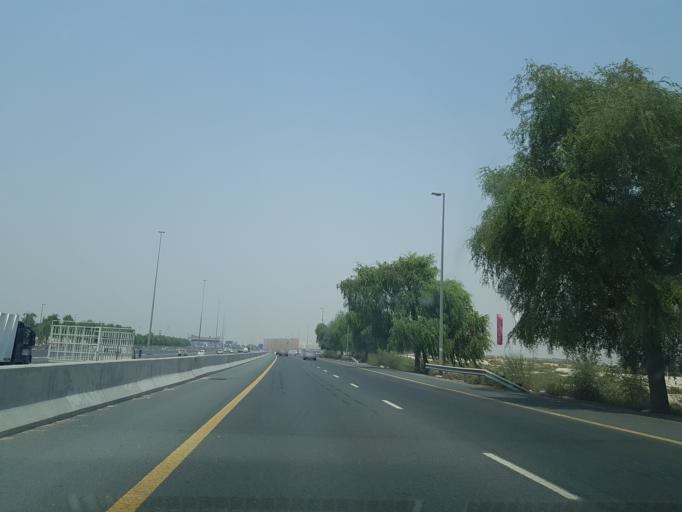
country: AE
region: Ash Shariqah
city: Sharjah
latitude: 25.1282
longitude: 55.3754
